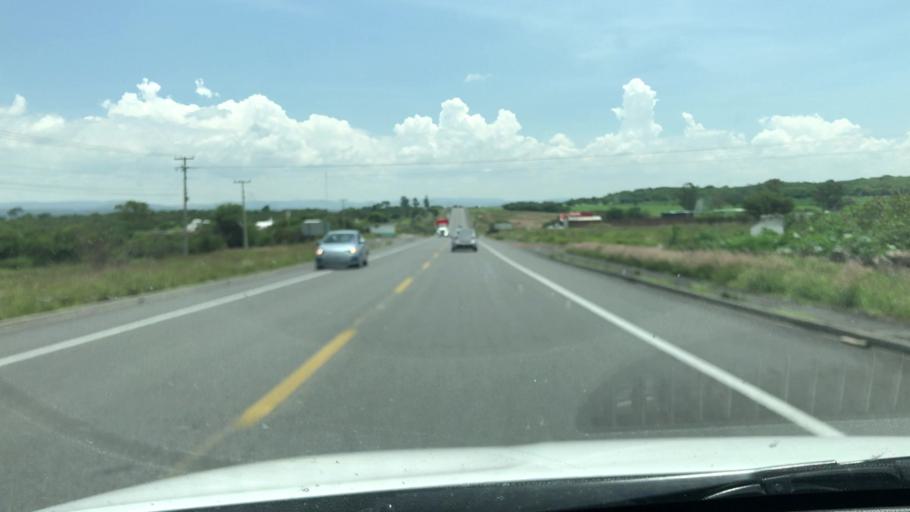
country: MX
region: Jalisco
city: Degollado
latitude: 20.3526
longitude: -102.1546
